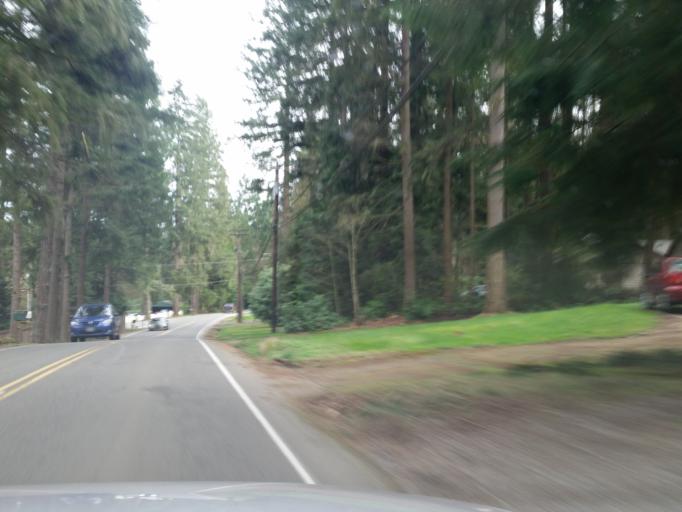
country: US
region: Washington
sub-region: King County
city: Cottage Lake
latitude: 47.7501
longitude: -122.1088
